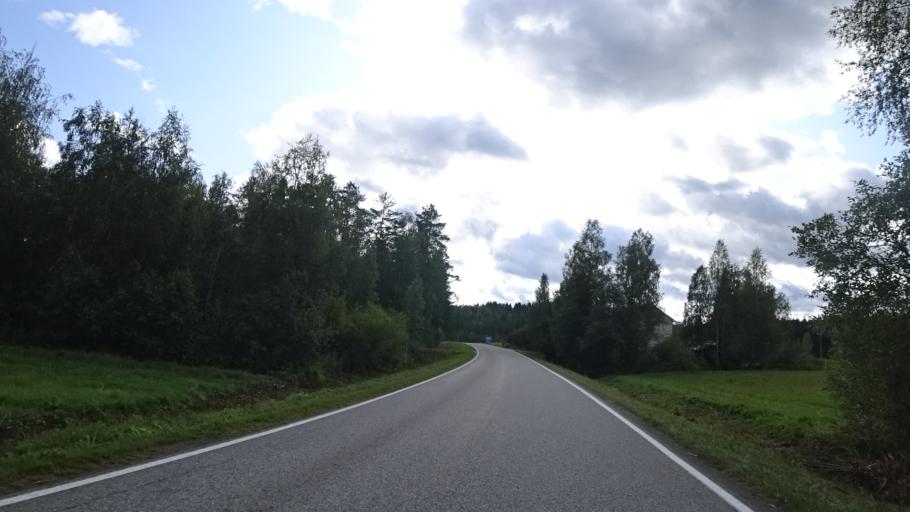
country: RU
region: Republic of Karelia
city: Vyartsilya
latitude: 62.2164
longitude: 30.6046
